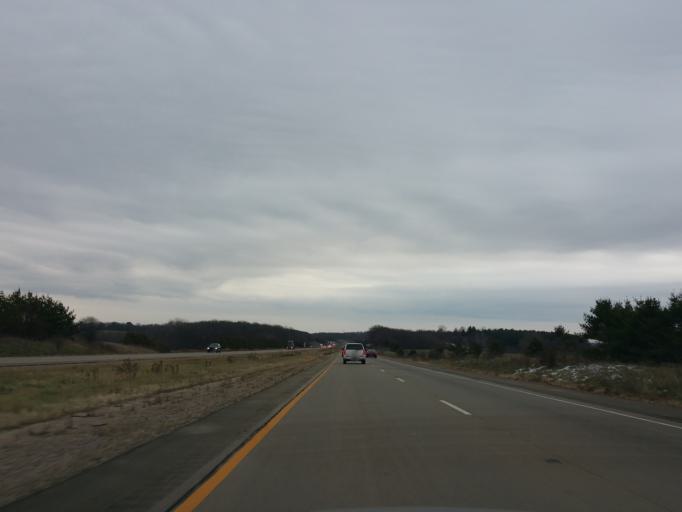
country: US
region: Wisconsin
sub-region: Sauk County
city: Baraboo
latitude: 43.5551
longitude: -89.7013
